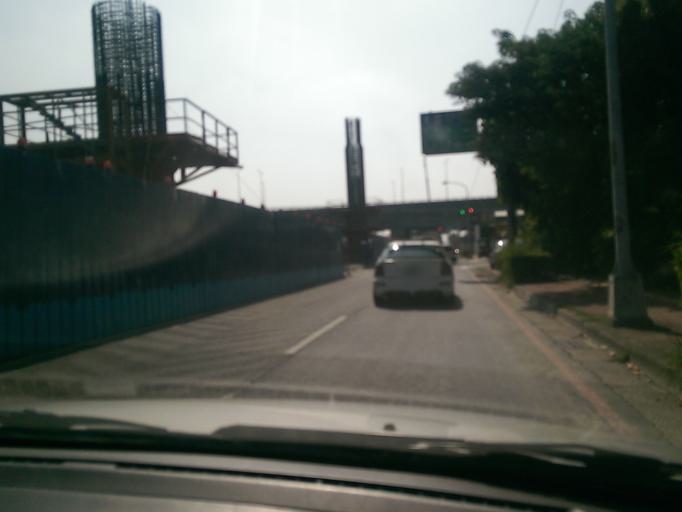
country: TW
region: Taiwan
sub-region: Taichung City
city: Taichung
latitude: 24.1164
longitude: 120.6431
